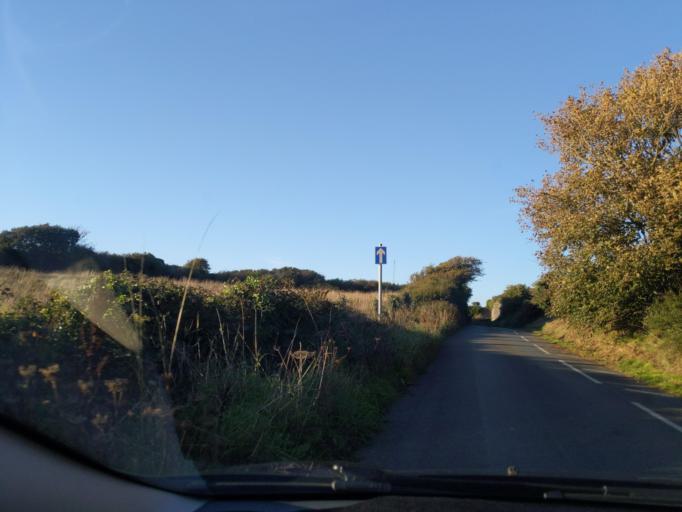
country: GB
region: England
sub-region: Plymouth
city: Plymouth
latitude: 50.3535
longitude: -4.1208
